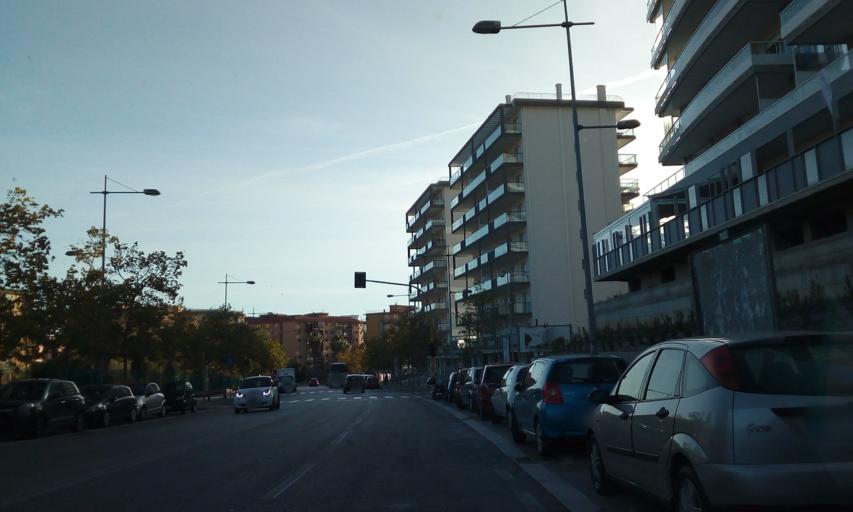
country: IT
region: Campania
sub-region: Provincia di Salerno
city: Capezzano Inferiore
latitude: 40.6859
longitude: 14.7751
